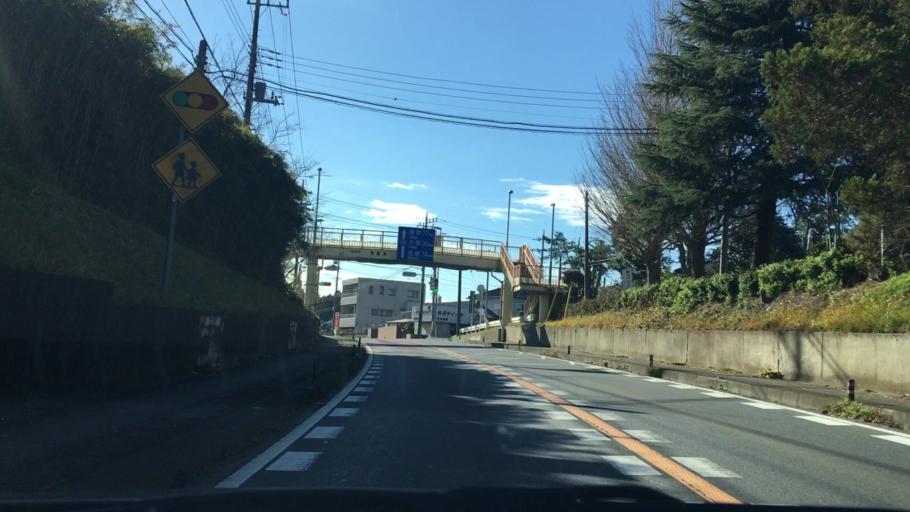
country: JP
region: Chiba
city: Sawara
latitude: 35.8309
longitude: 140.4142
